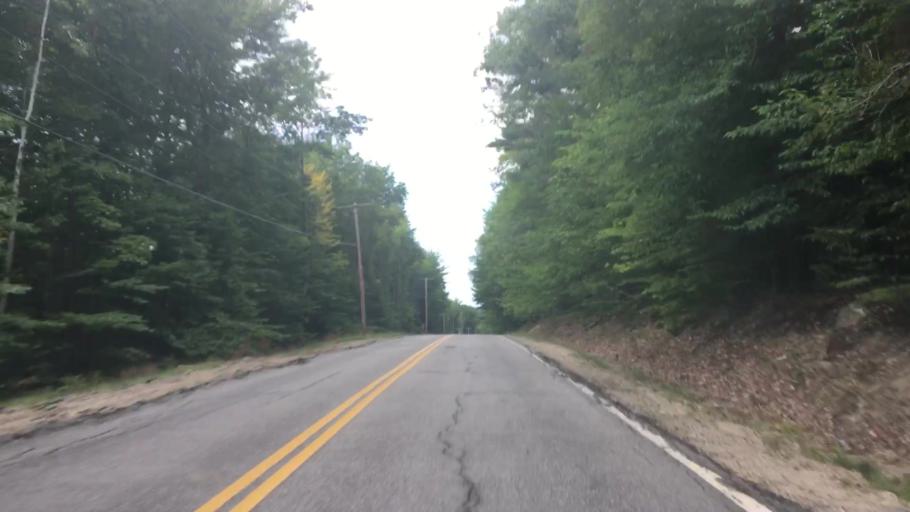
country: US
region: Maine
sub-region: Oxford County
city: Oxford
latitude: 44.0232
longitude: -70.5292
